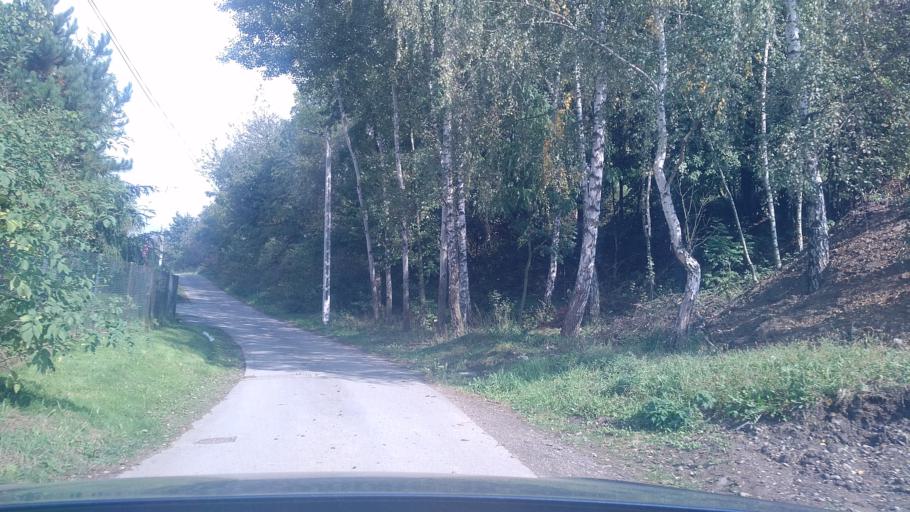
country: PL
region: Lesser Poland Voivodeship
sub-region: Powiat krakowski
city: Wielka Wies
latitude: 50.1364
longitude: 19.8384
